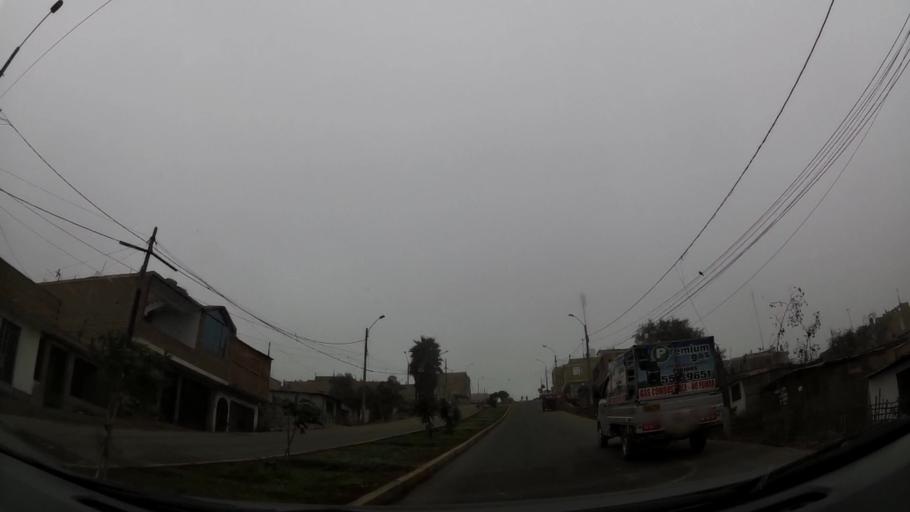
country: PE
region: Lima
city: Ventanilla
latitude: -11.8322
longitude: -77.1065
